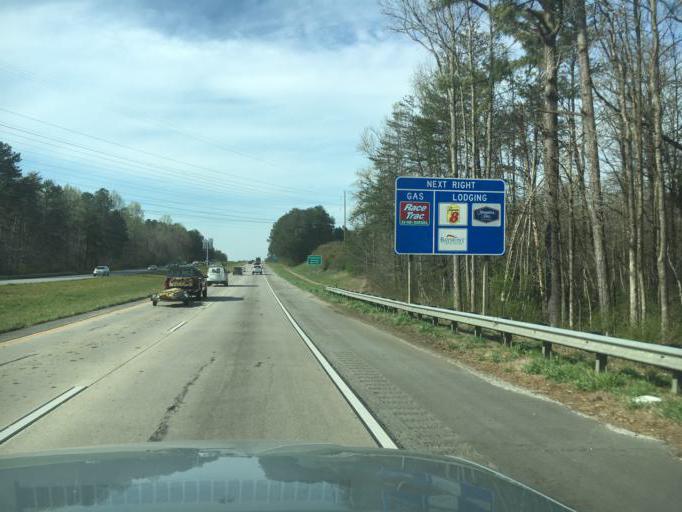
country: US
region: Georgia
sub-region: Habersham County
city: Cornelia
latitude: 34.5270
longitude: -83.5407
